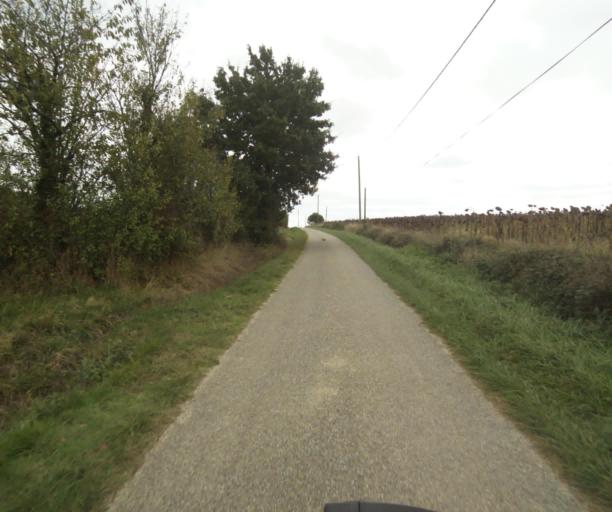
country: FR
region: Midi-Pyrenees
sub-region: Departement du Tarn-et-Garonne
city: Beaumont-de-Lomagne
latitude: 43.8563
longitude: 1.0613
